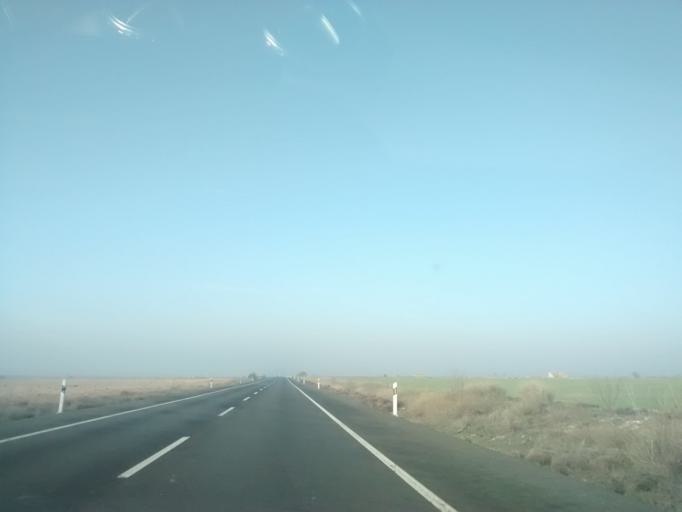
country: ES
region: Aragon
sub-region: Provincia de Huesca
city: Saidi / Zaidin
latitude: 41.5172
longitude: 0.2391
